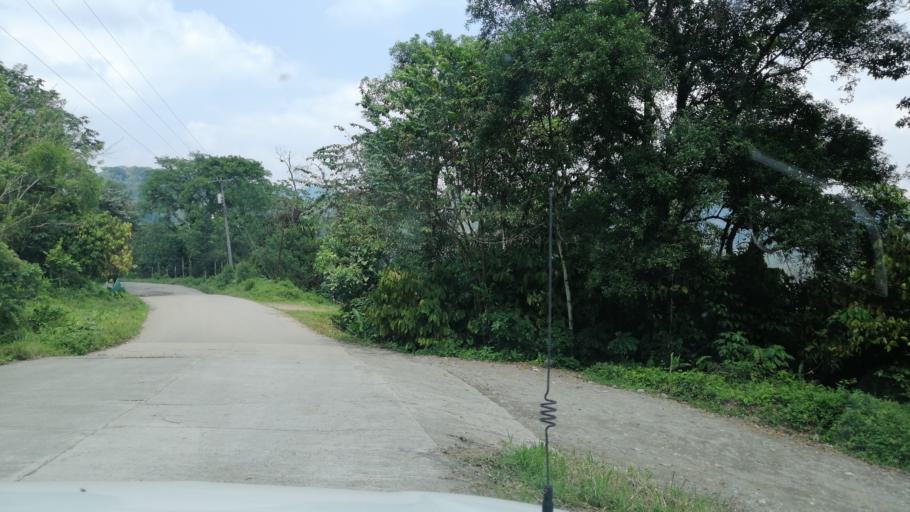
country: MX
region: Chiapas
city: Ostuacan
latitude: 17.3968
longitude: -93.3311
